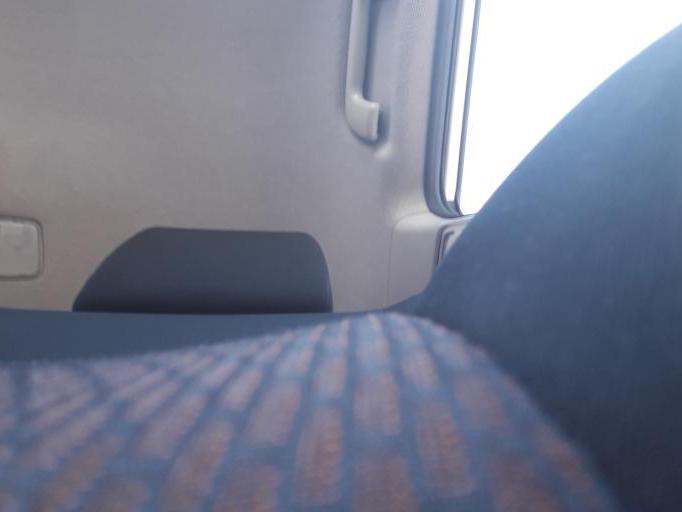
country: ZA
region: Gauteng
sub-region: City of Johannesburg Metropolitan Municipality
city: Diepsloot
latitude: -26.0183
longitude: 28.0042
